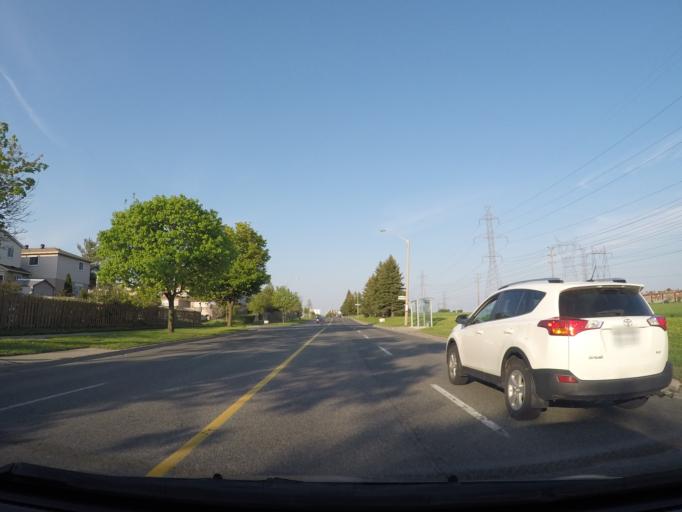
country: CA
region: Ontario
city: Markham
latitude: 43.8193
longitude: -79.2653
